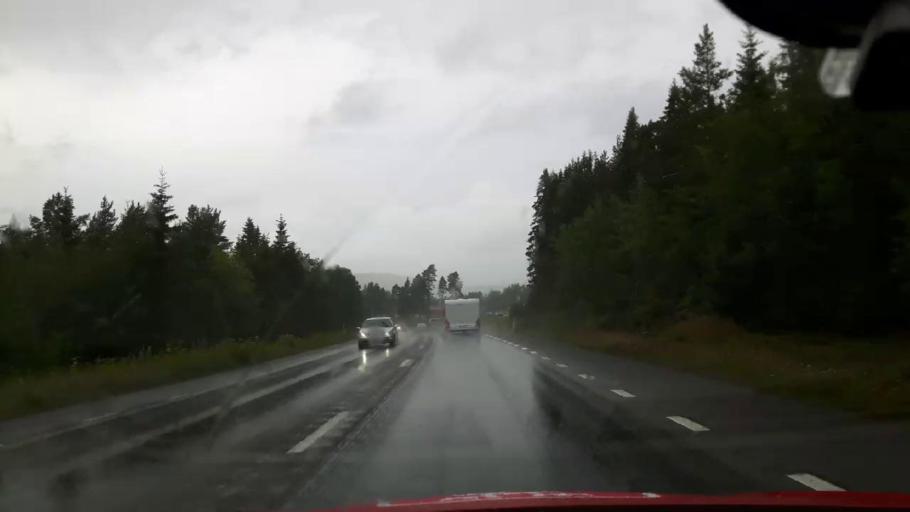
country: SE
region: Jaemtland
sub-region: Are Kommun
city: Jarpen
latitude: 63.3404
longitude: 13.4902
